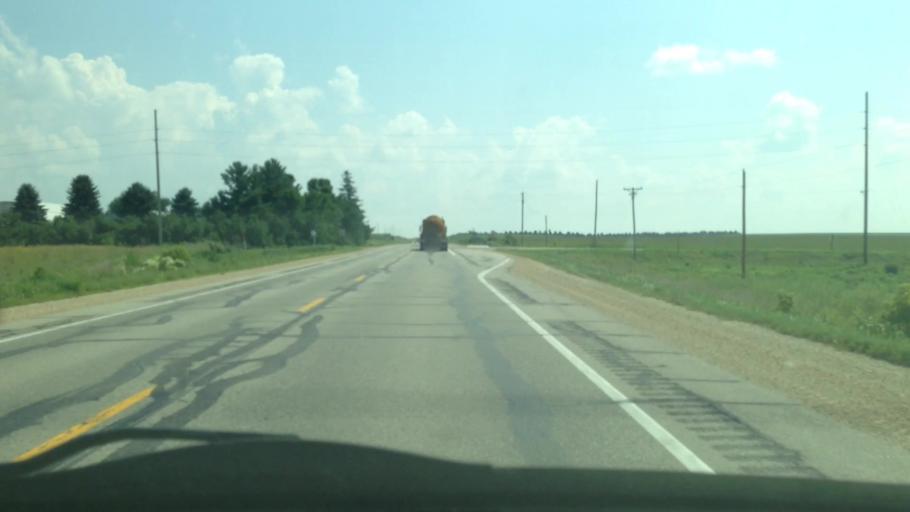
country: US
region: Iowa
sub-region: Chickasaw County
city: New Hampton
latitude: 43.2002
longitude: -92.2983
